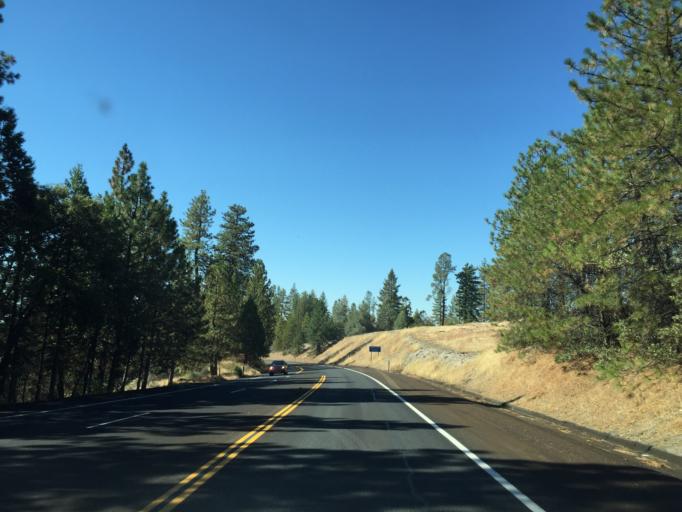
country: US
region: California
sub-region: Tuolumne County
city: Twain Harte
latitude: 38.0260
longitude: -120.2367
